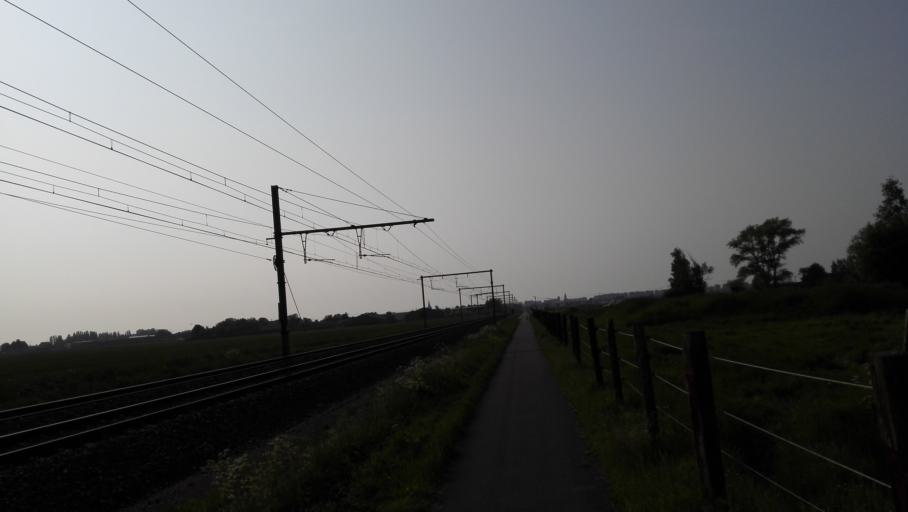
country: BE
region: Flanders
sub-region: Provincie West-Vlaanderen
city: Zuienkerke
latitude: 51.2939
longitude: 3.1639
